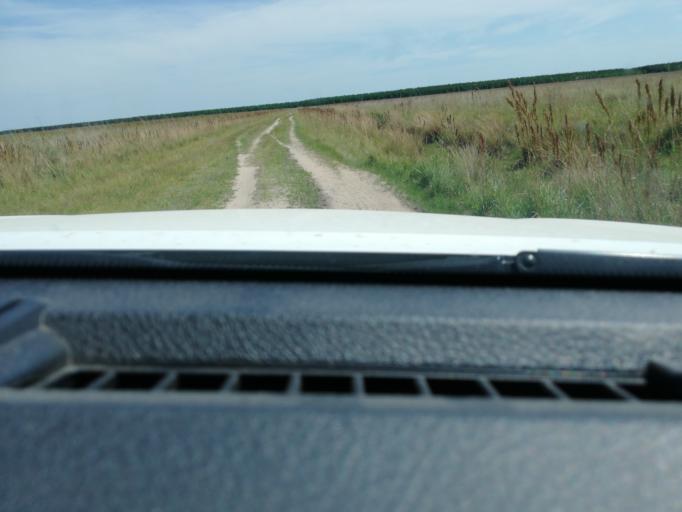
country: AR
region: Corrientes
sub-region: Departamento de San Miguel
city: San Miguel
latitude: -28.0493
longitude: -57.4555
